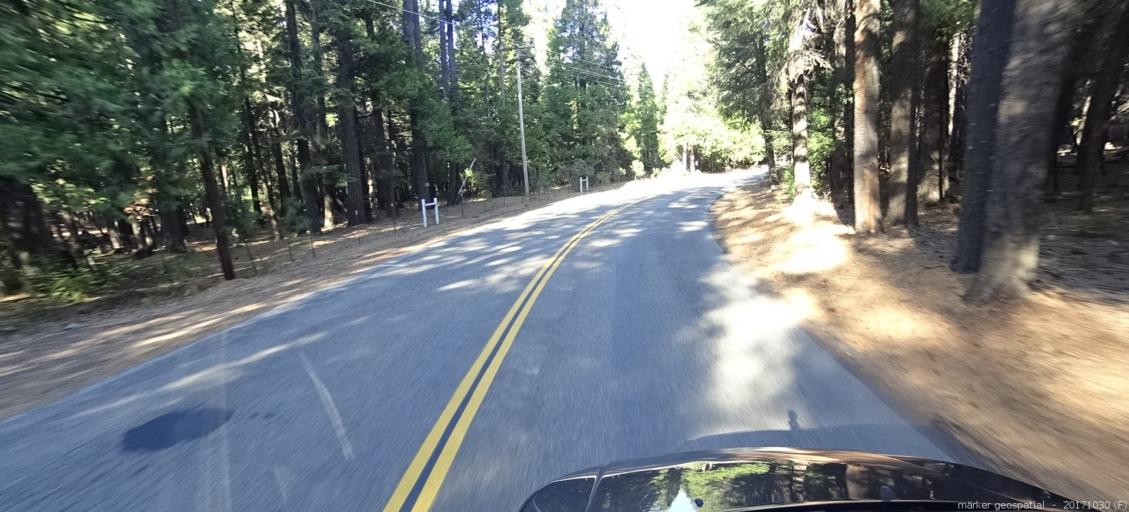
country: US
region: California
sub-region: Shasta County
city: Shingletown
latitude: 40.5232
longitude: -121.7500
